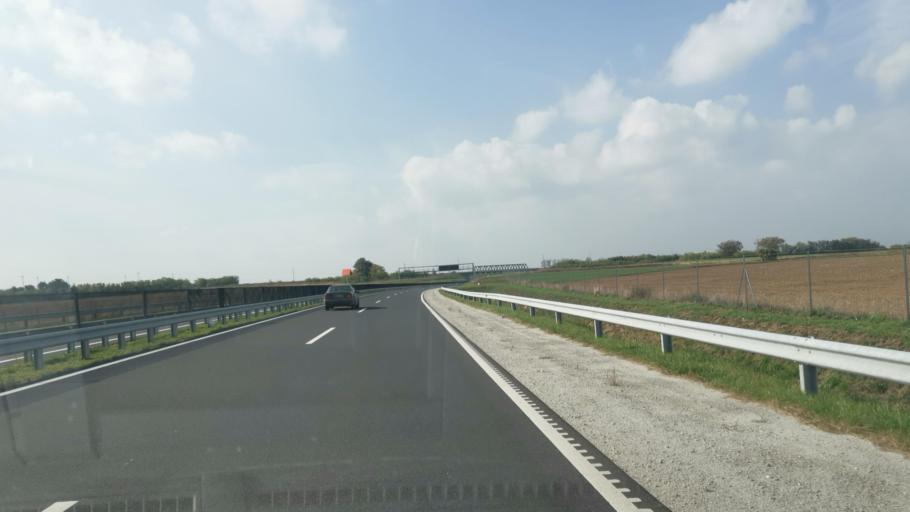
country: HU
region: Gyor-Moson-Sopron
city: Nagycenk
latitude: 47.5818
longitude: 16.7318
